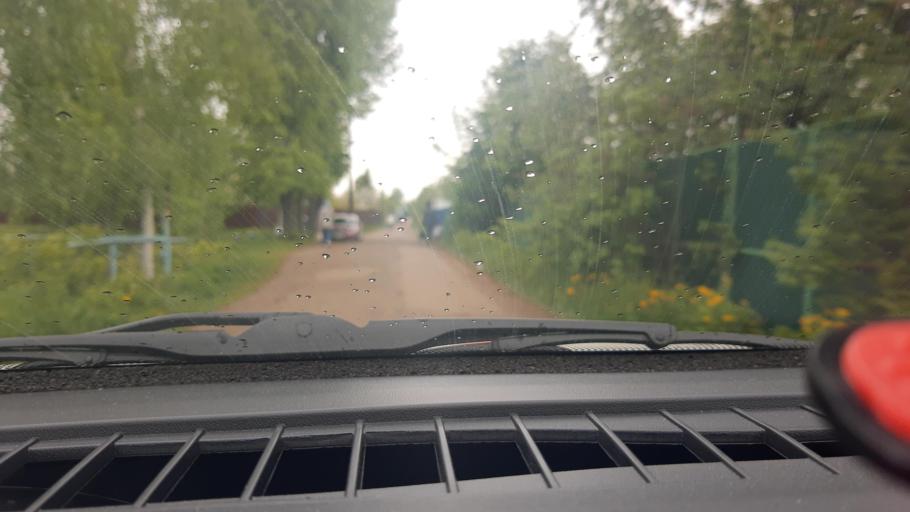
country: RU
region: Nizjnij Novgorod
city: Burevestnik
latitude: 56.2163
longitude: 43.8516
